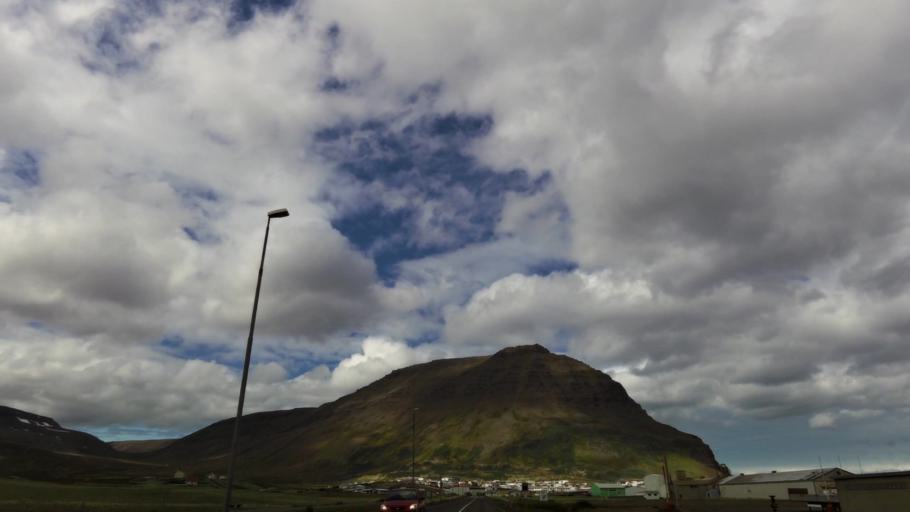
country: IS
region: Westfjords
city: Isafjoerdur
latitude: 66.1504
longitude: -23.2453
